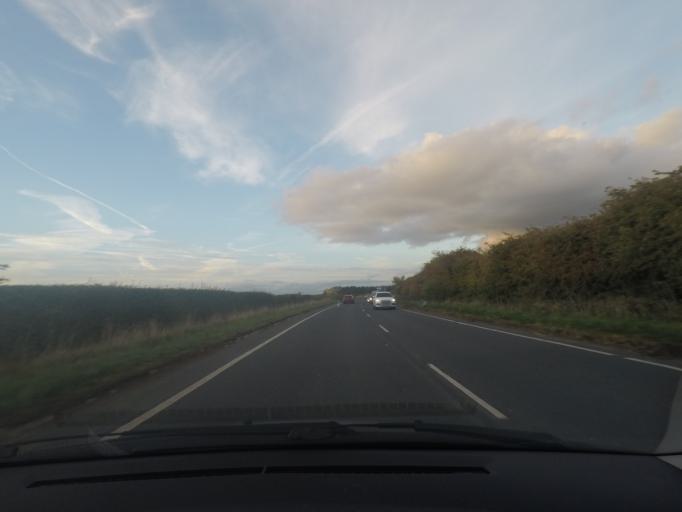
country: GB
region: England
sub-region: City of York
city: Nether Poppleton
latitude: 53.9613
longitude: -1.1506
